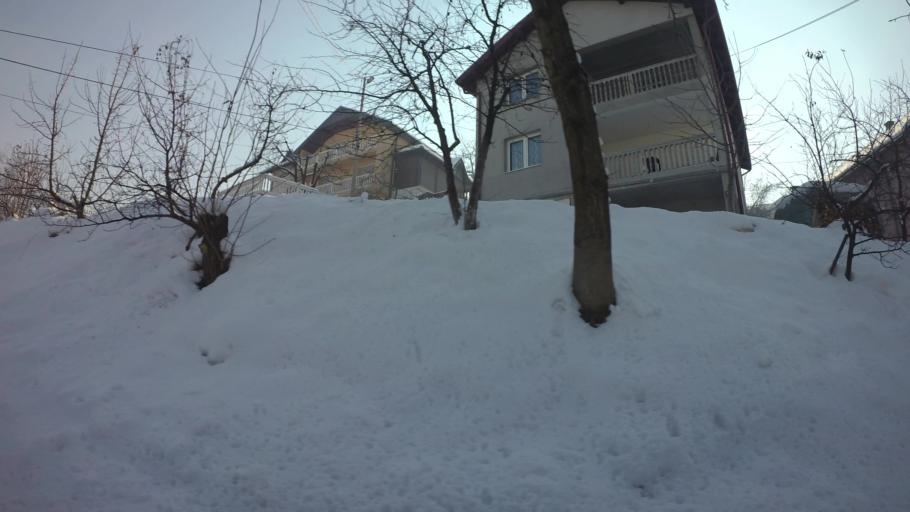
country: BA
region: Federation of Bosnia and Herzegovina
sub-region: Kanton Sarajevo
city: Sarajevo
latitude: 43.8431
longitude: 18.3882
